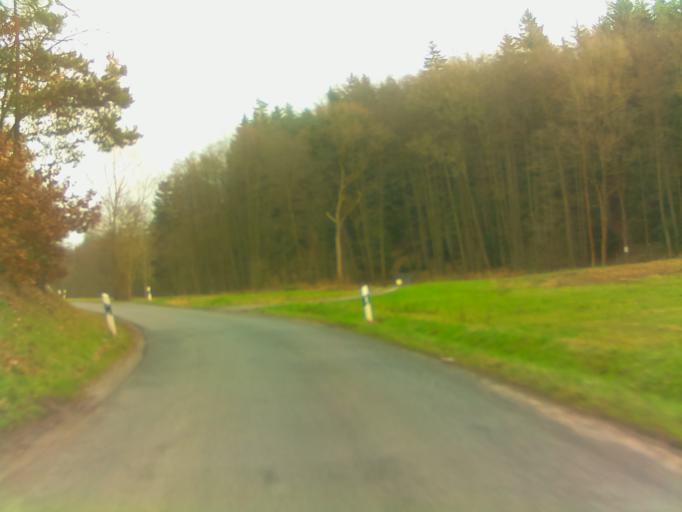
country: DE
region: Thuringia
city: Grosspurschutz
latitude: 50.8227
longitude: 11.6142
